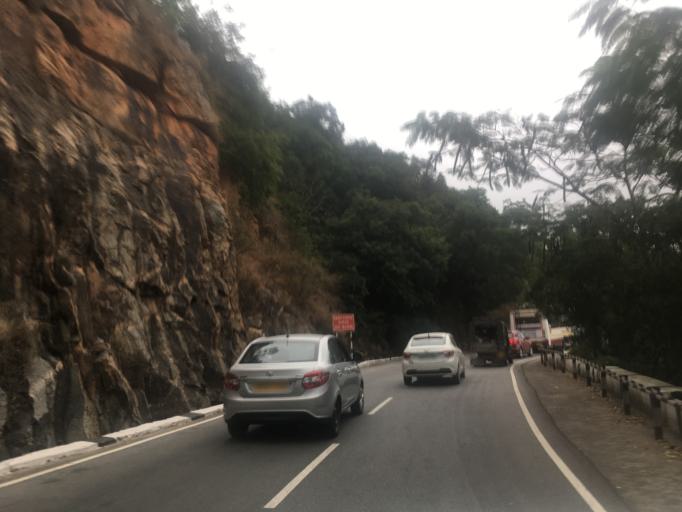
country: IN
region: Andhra Pradesh
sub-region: Chittoor
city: Tirumala
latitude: 13.6677
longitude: 79.3497
